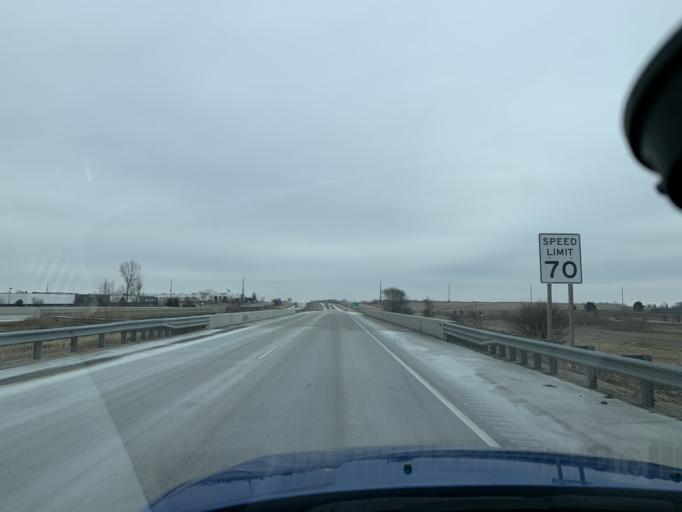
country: US
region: Wisconsin
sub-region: Dane County
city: Sun Prairie
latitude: 43.2005
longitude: -89.1987
